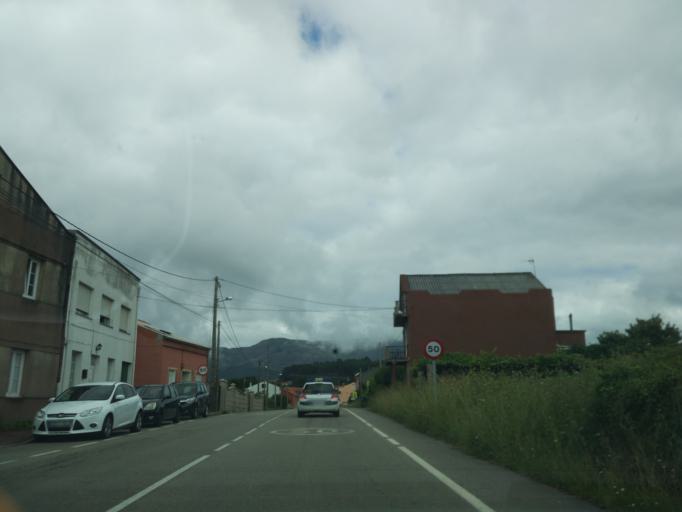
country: ES
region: Galicia
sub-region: Provincia da Coruna
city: Boiro
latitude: 42.6452
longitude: -8.8732
